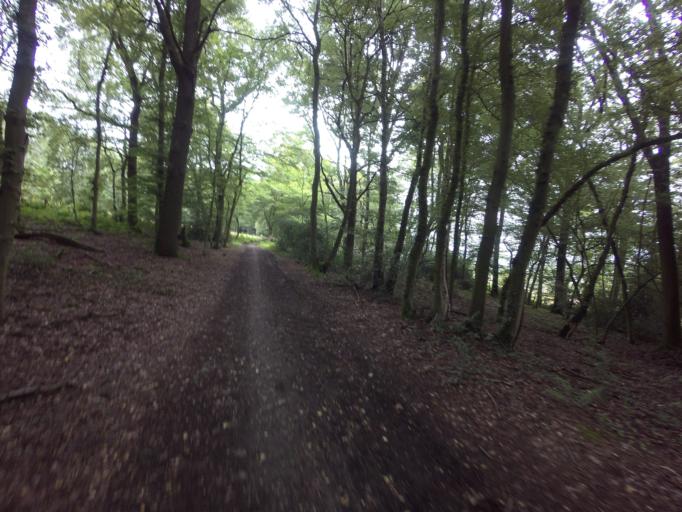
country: BE
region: Wallonia
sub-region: Province de Liege
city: Plombieres
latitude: 50.7732
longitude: 5.9502
